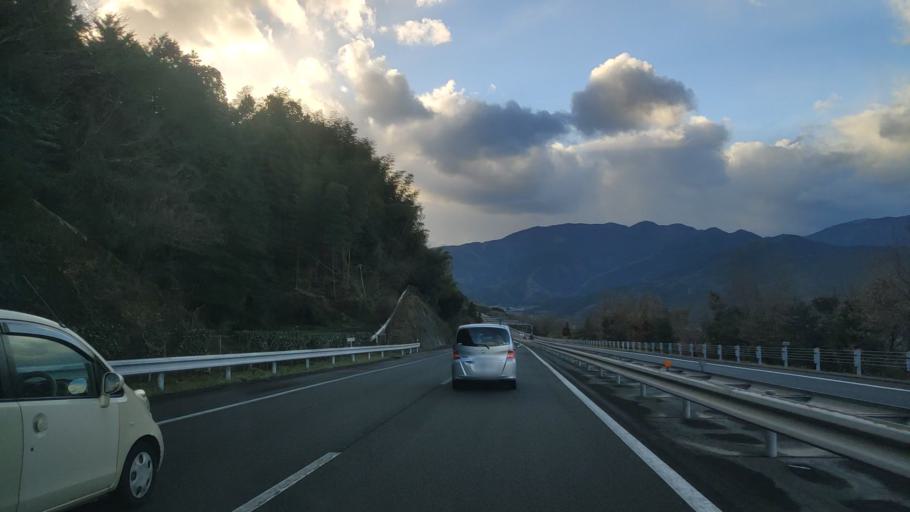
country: JP
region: Ehime
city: Saijo
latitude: 33.8560
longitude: 133.0368
